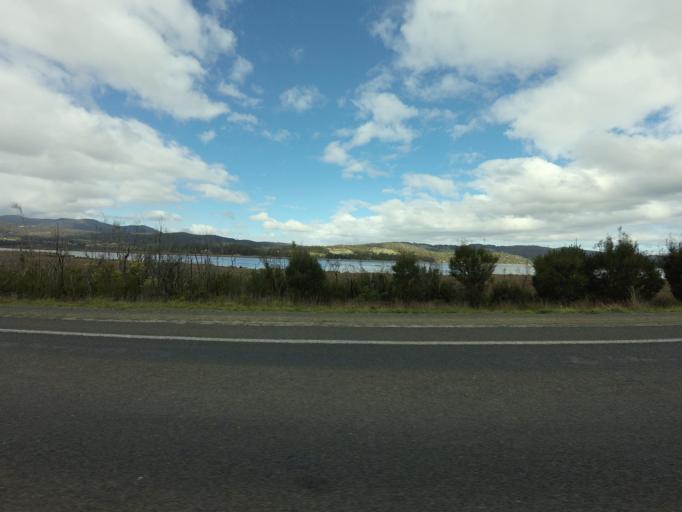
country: AU
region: Tasmania
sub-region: Huon Valley
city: Franklin
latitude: -43.1159
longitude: 146.9931
